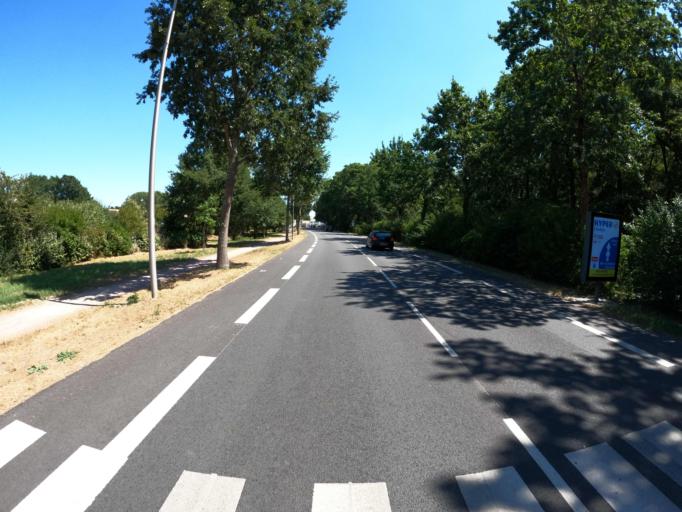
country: FR
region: Pays de la Loire
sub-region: Departement de la Vendee
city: Challans
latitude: 46.8390
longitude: -1.8899
